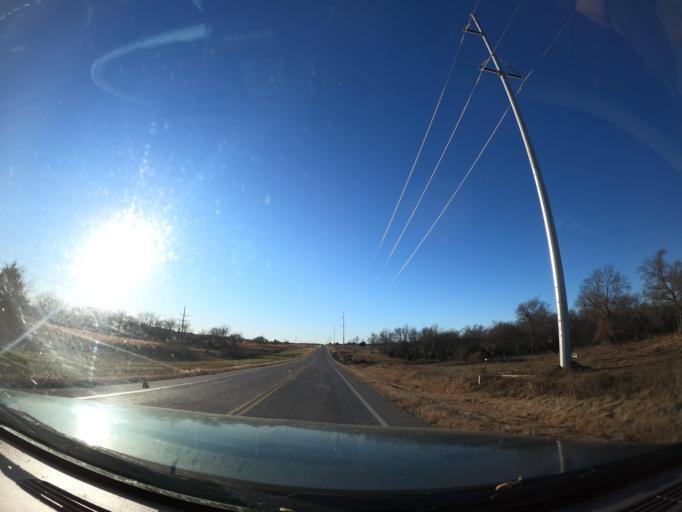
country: US
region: Oklahoma
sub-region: Latimer County
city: Wilburton
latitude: 34.9129
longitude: -95.4033
